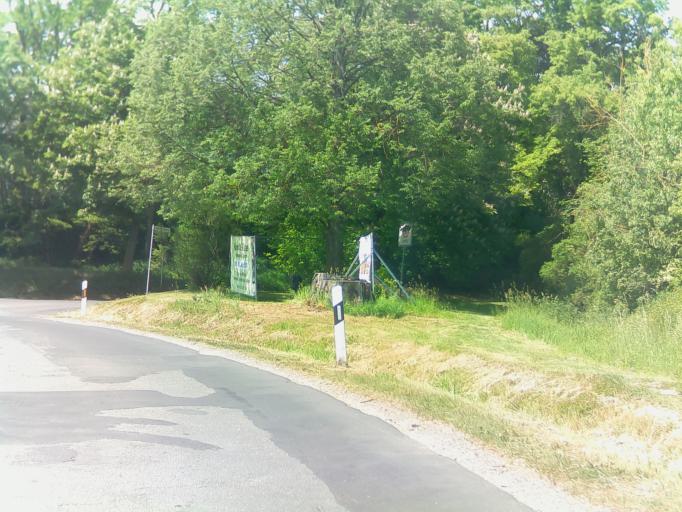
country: DE
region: Bavaria
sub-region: Regierungsbezirk Unterfranken
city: Arnstein
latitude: 49.9785
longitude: 9.9612
